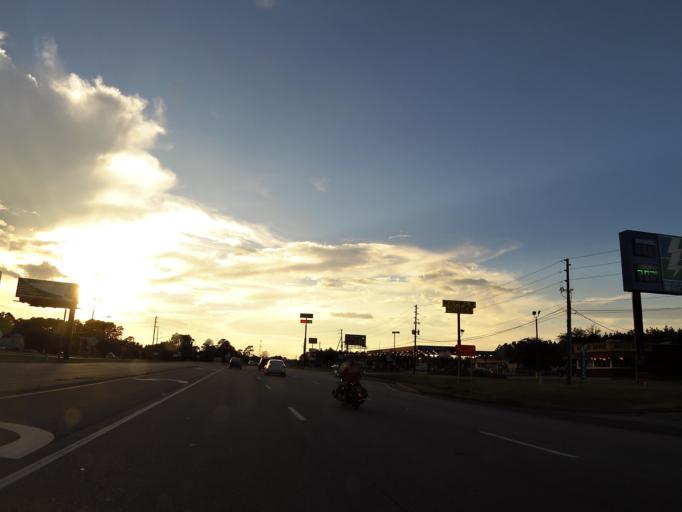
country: US
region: Georgia
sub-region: Camden County
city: Kingsland
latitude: 30.7920
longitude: -81.6629
